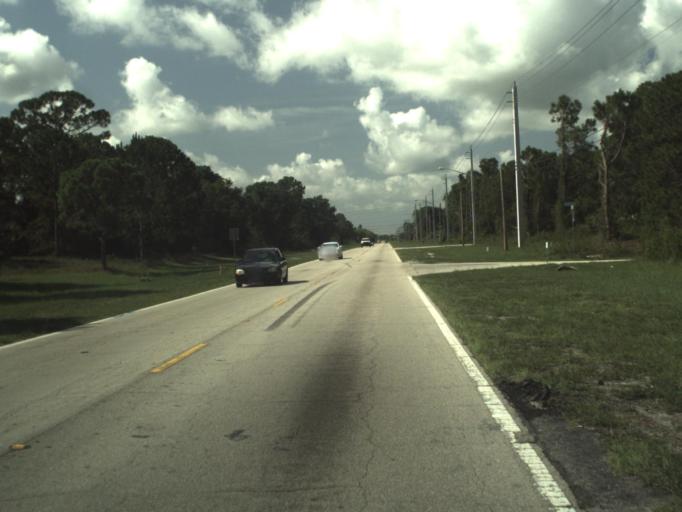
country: US
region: Florida
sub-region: Saint Lucie County
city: Port Saint Lucie
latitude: 27.2460
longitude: -80.3769
